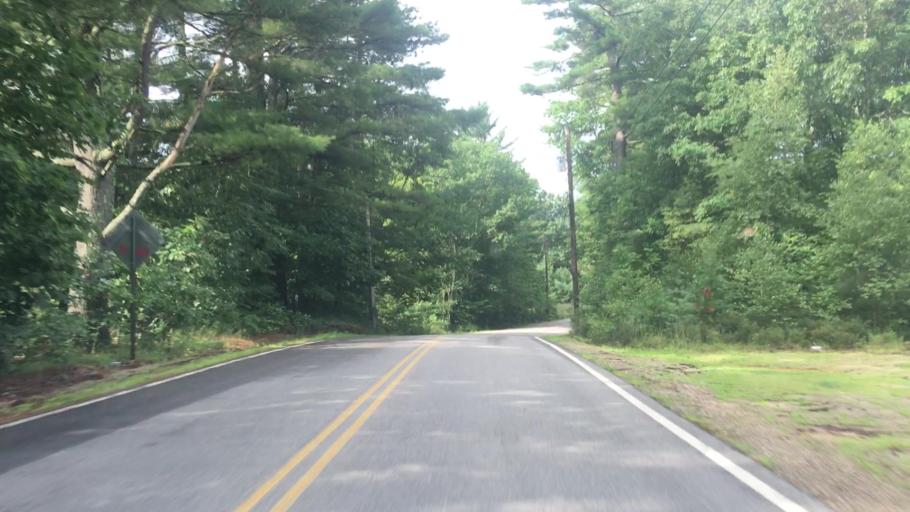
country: US
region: New Hampshire
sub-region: Strafford County
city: Farmington
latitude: 43.3772
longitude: -71.0393
